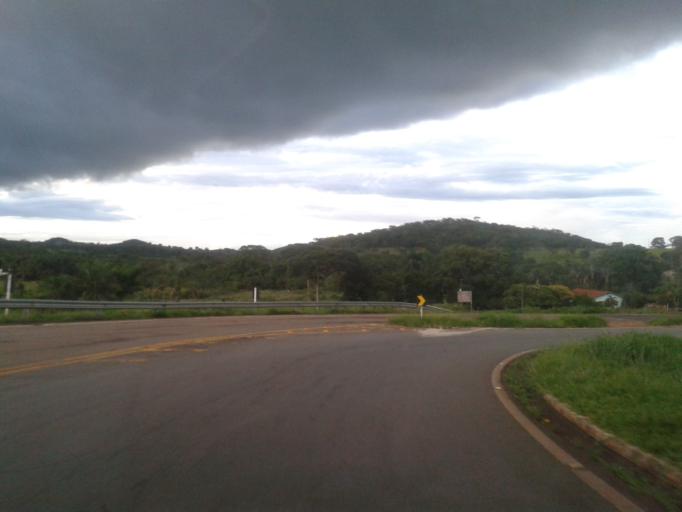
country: BR
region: Goias
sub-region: Morrinhos
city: Morrinhos
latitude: -17.7270
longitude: -49.1554
